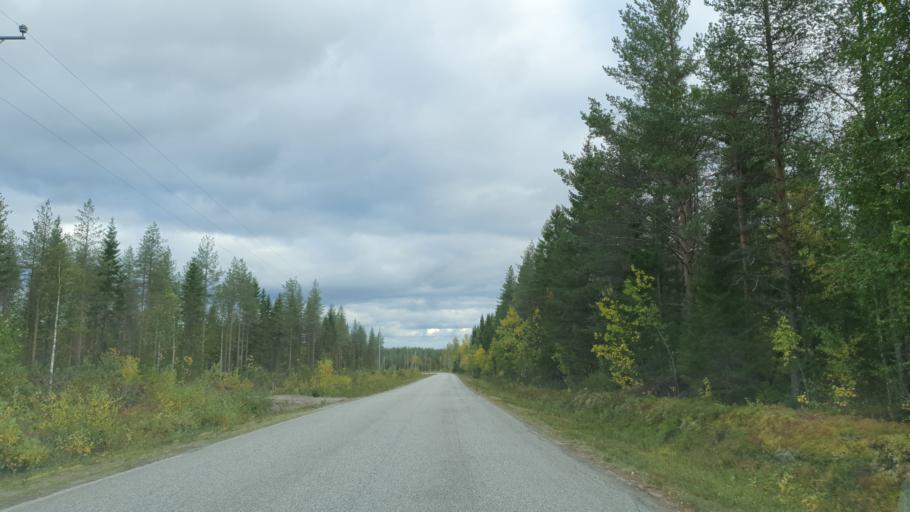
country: FI
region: Kainuu
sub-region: Kehys-Kainuu
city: Kuhmo
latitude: 63.9509
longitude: 29.8067
